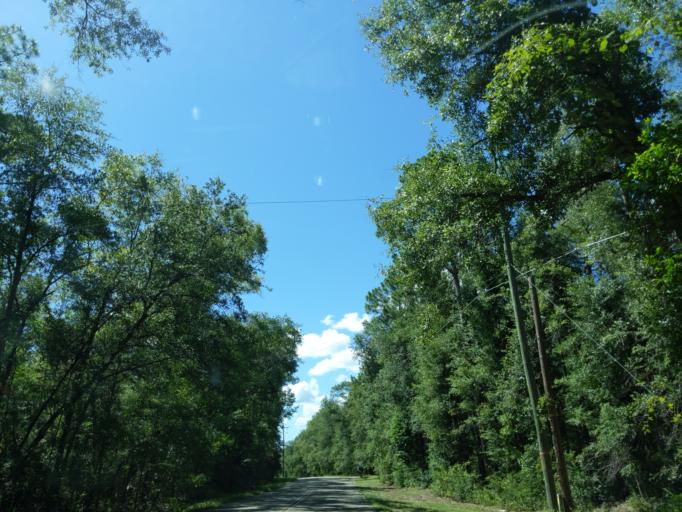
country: US
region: Florida
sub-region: Leon County
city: Tallahassee
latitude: 30.4005
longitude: -84.3422
